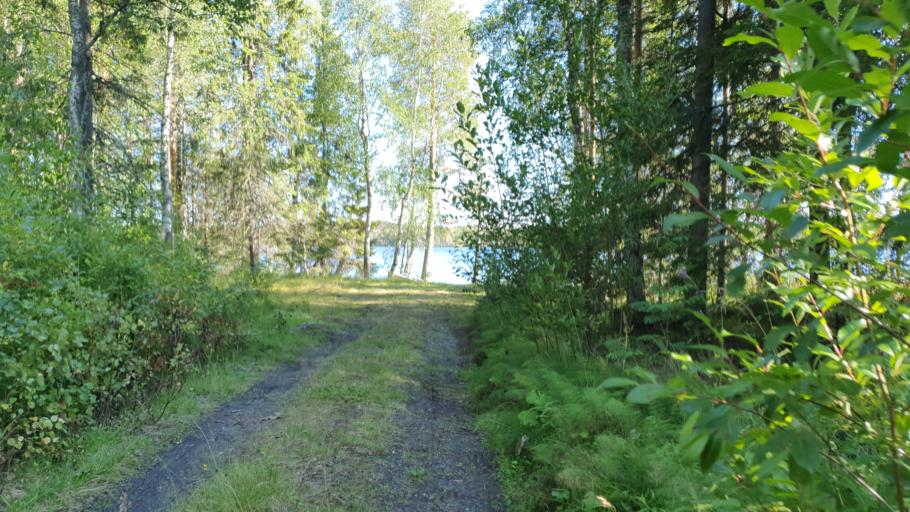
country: FI
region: Kainuu
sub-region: Kehys-Kainuu
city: Kuhmo
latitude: 64.1256
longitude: 29.4777
